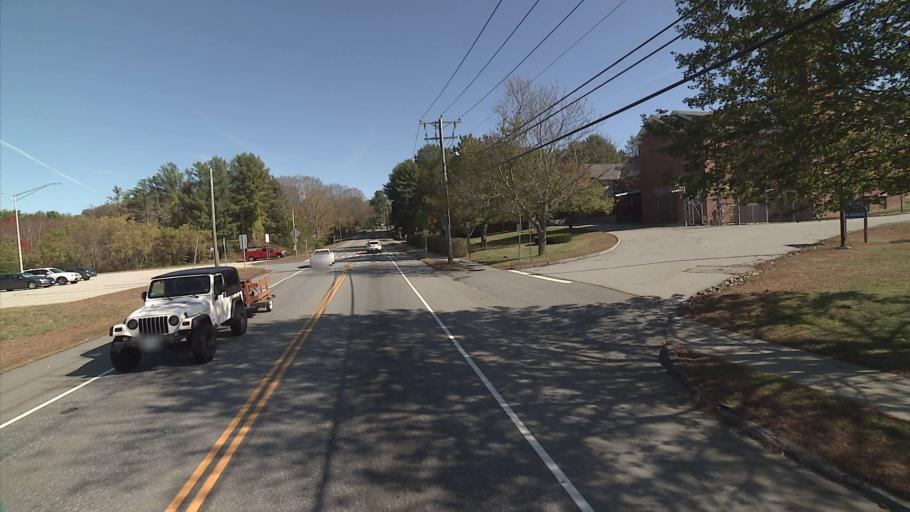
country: US
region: Connecticut
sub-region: Windham County
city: East Brooklyn
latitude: 41.7856
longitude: -71.9551
